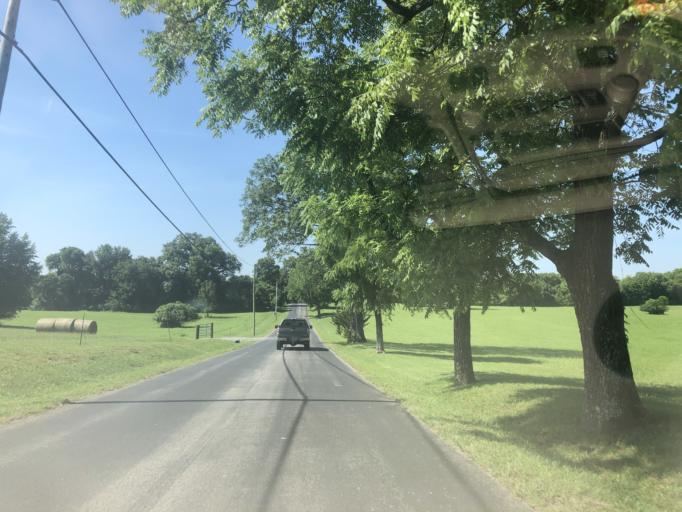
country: US
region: Tennessee
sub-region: Davidson County
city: Lakewood
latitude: 36.2109
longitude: -86.6187
